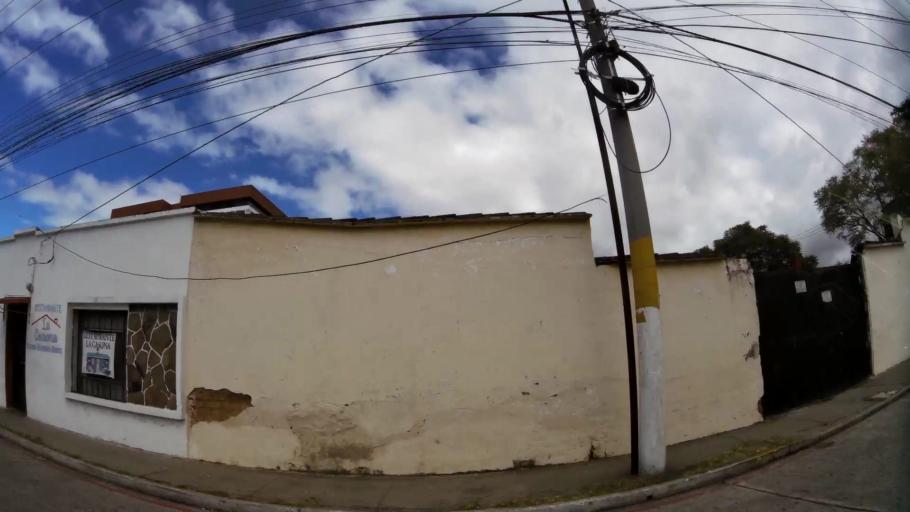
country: GT
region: Guatemala
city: Guatemala City
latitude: 14.6071
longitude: -90.5133
